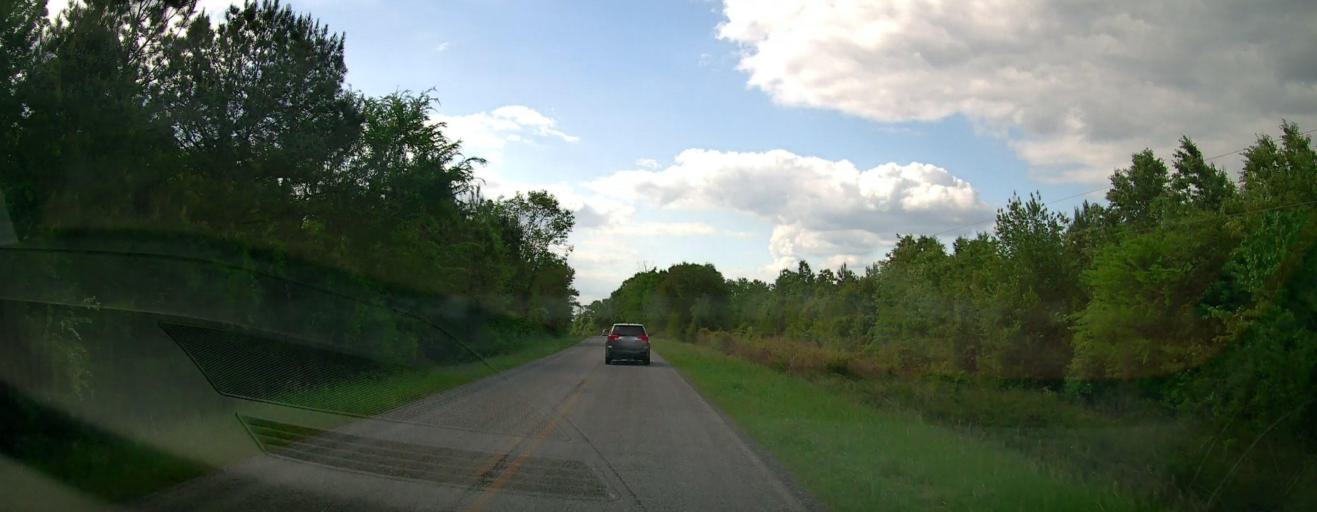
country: US
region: Georgia
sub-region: Laurens County
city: East Dublin
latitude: 32.6912
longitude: -82.9004
